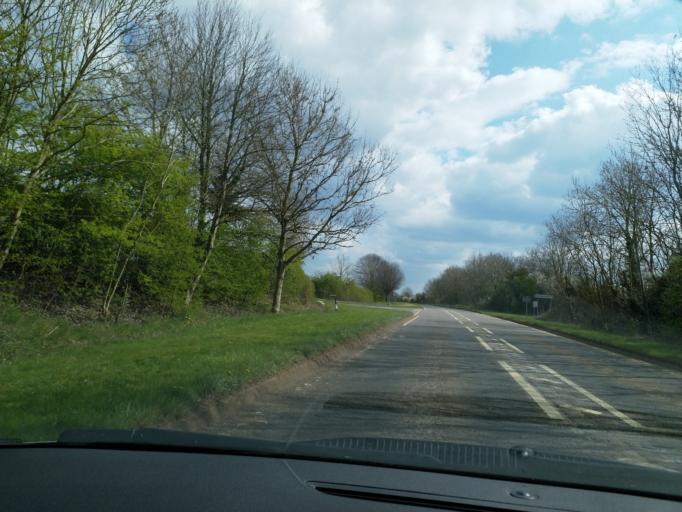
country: GB
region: England
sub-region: Oxfordshire
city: Hanwell
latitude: 52.1060
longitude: -1.3879
